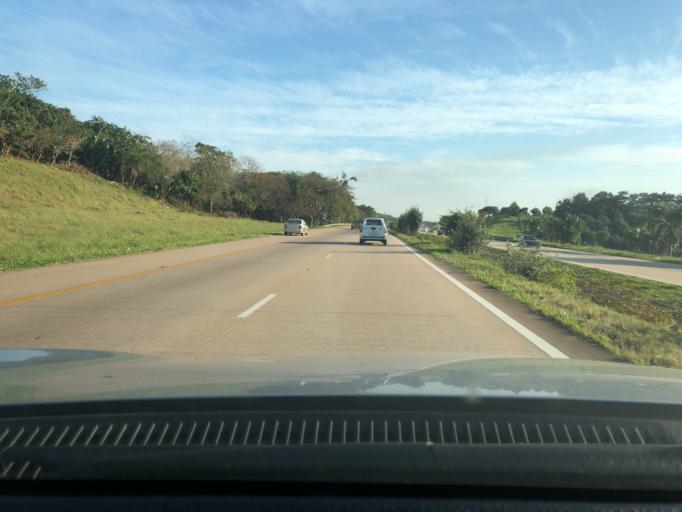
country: ZA
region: KwaZulu-Natal
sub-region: iLembe District Municipality
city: Ballitoville
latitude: -29.4741
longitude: 31.2321
